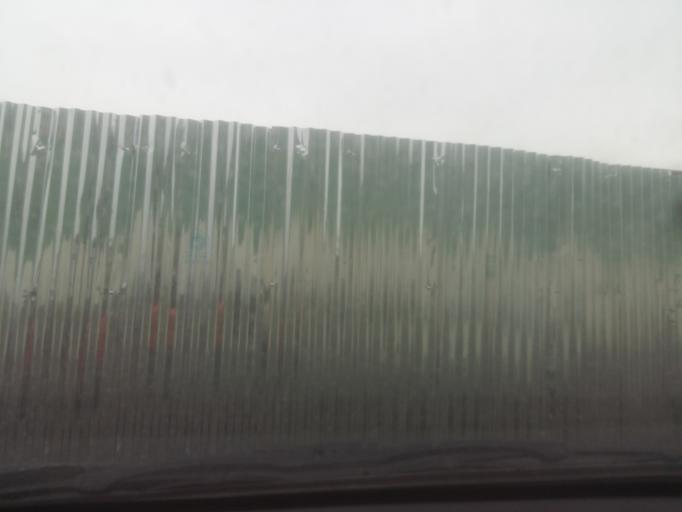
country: ET
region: Oromiya
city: Bishoftu
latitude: 8.8068
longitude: 38.8989
